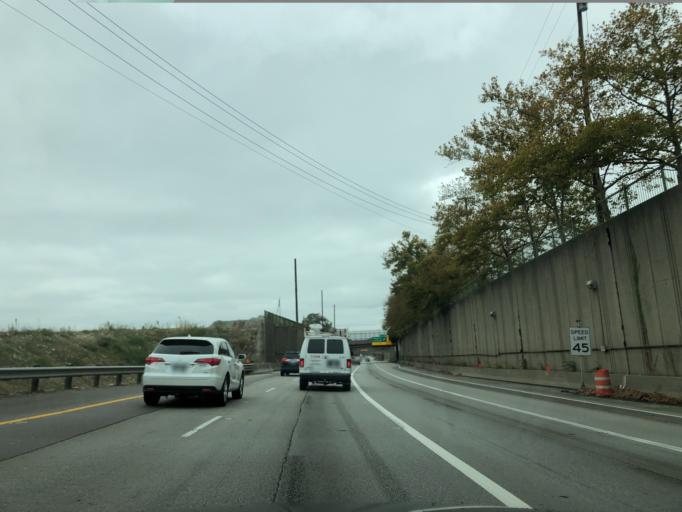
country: US
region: Ohio
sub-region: Hamilton County
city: Lockland
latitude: 39.2271
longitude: -84.4510
